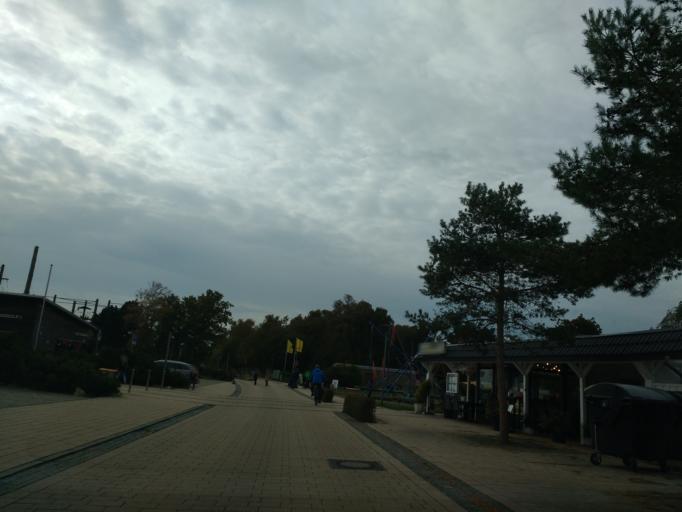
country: DE
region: Schleswig-Holstein
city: Gromitz
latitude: 54.1593
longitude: 10.9975
